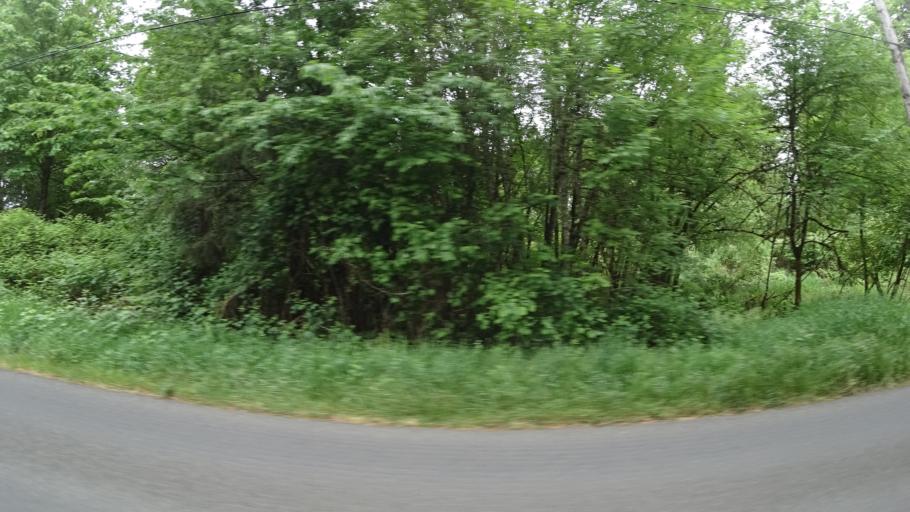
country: US
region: Oregon
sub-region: Washington County
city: Aloha
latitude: 45.4815
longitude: -122.9136
